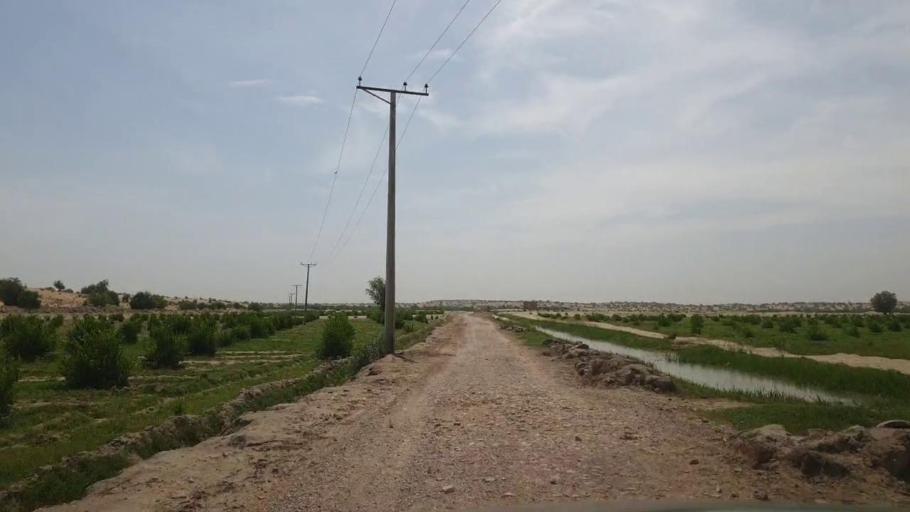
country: PK
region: Sindh
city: Bozdar
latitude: 27.0791
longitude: 69.0731
